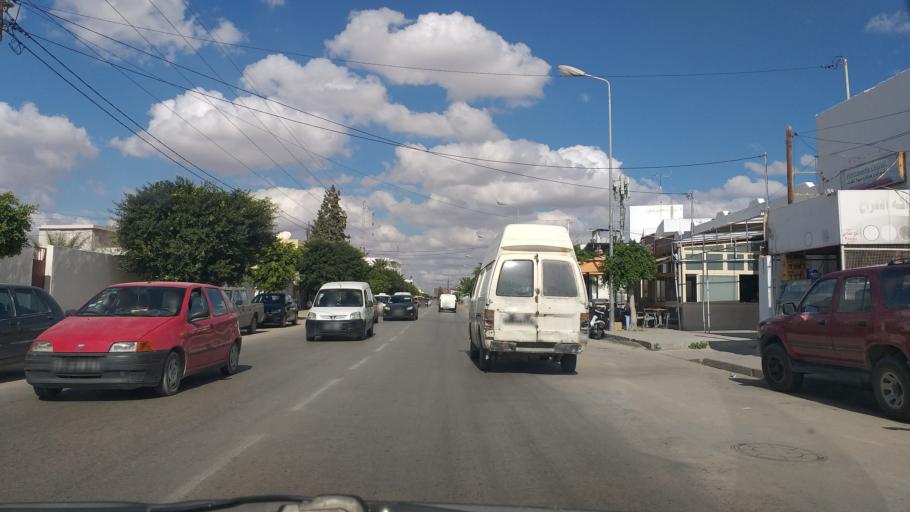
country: TN
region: Safaqis
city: Al Qarmadah
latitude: 34.7720
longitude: 10.7752
